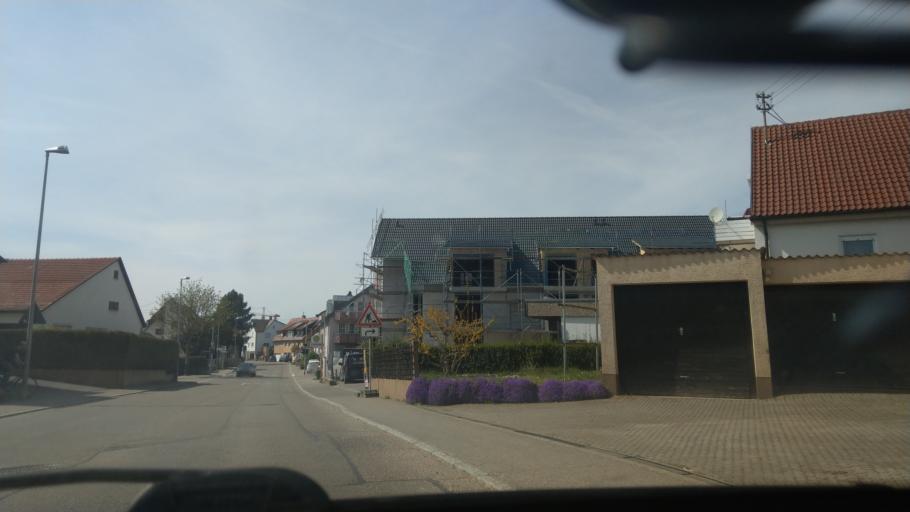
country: DE
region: Baden-Wuerttemberg
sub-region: Regierungsbezirk Stuttgart
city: Wolfschlugen
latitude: 48.6520
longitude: 9.2934
